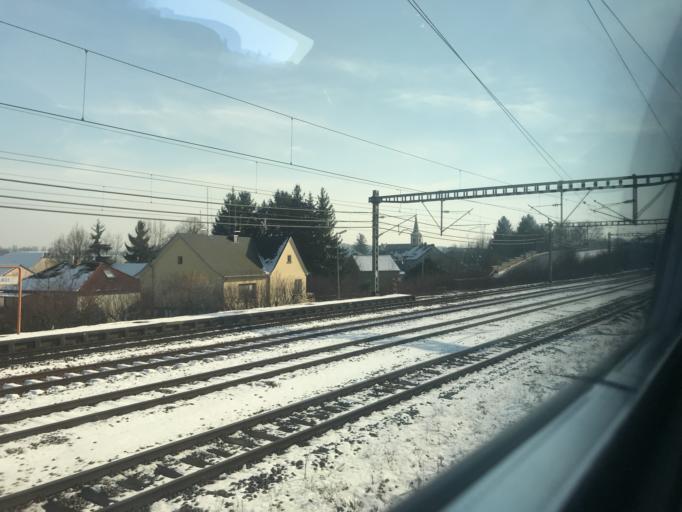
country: LU
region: Luxembourg
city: Schrassig
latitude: 49.6036
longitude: 6.2579
